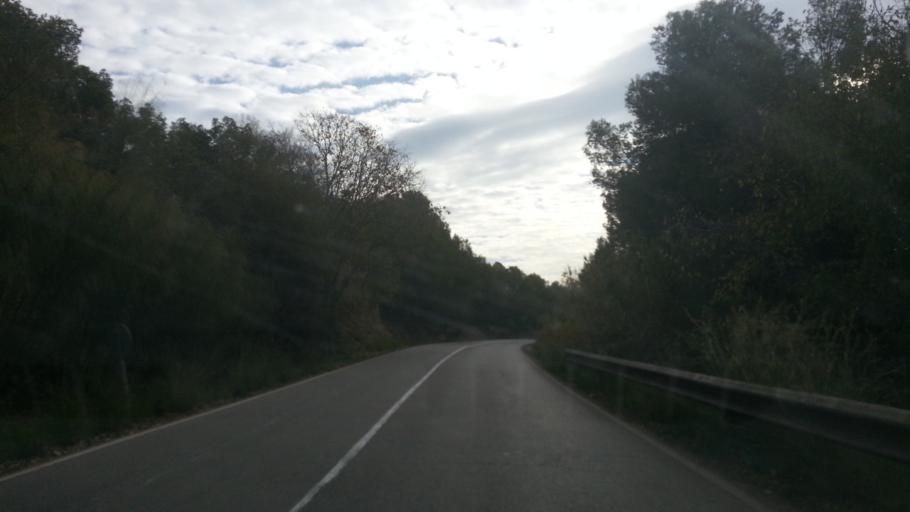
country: ES
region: Catalonia
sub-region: Provincia de Barcelona
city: Sant Pere de Ribes
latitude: 41.2549
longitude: 1.7817
